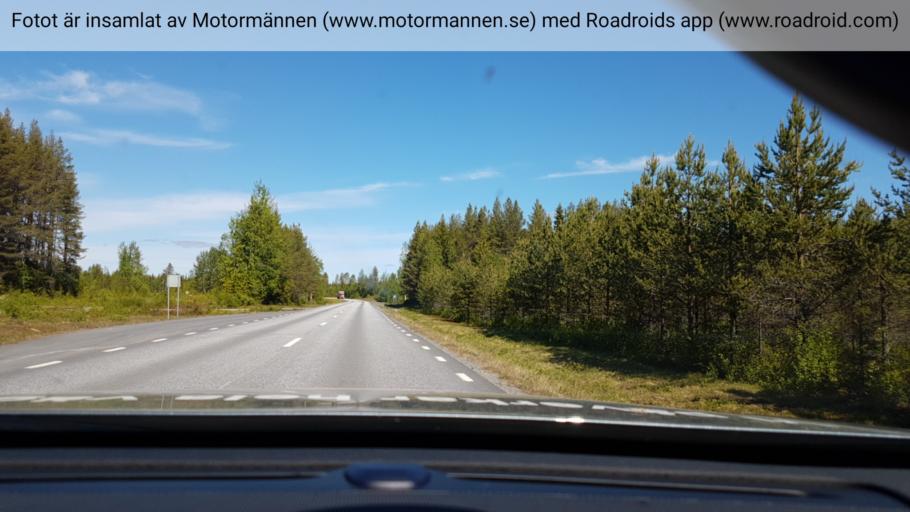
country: SE
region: Vaesterbotten
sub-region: Vilhelmina Kommun
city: Vilhelmina
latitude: 64.4982
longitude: 16.7778
